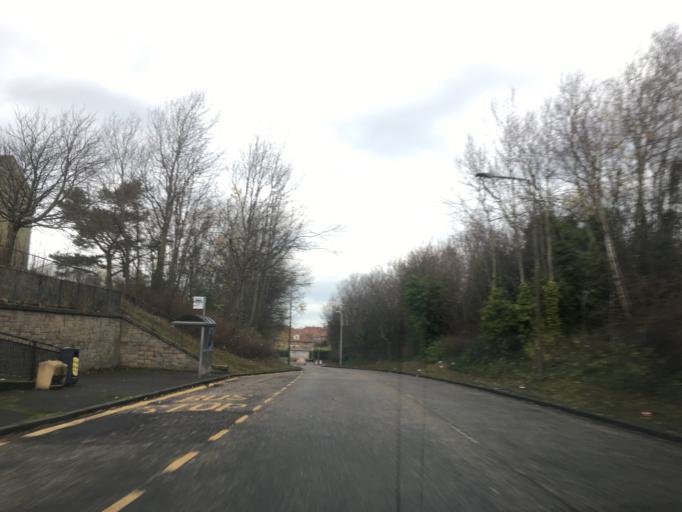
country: GB
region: Scotland
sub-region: Edinburgh
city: Colinton
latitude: 55.9198
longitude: -3.2760
